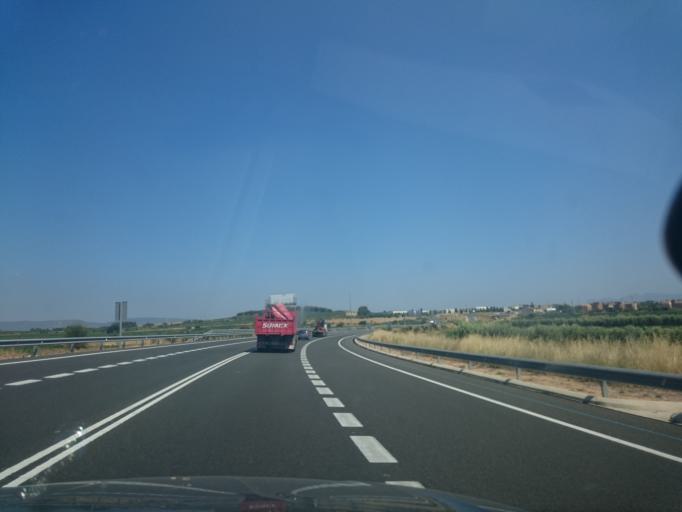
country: ES
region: Catalonia
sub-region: Provincia de Barcelona
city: La Granada
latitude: 41.3703
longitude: 1.7114
